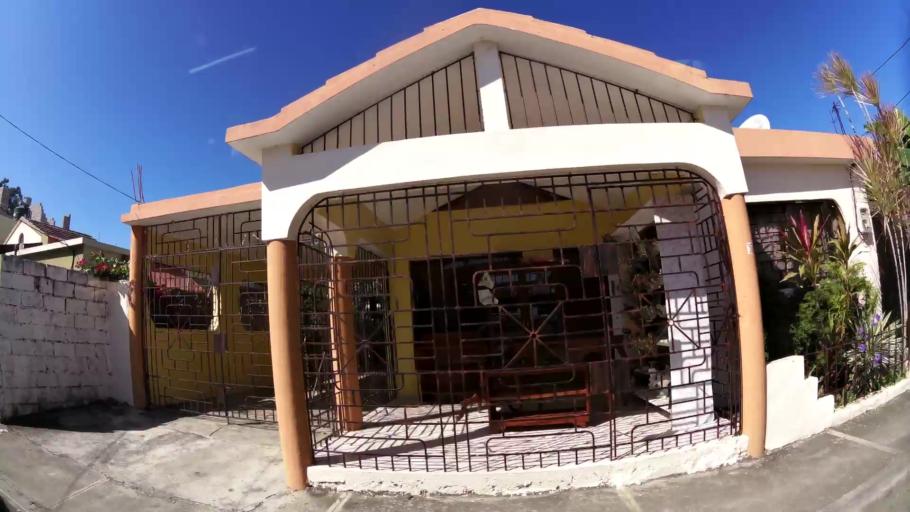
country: DO
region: San Cristobal
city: San Cristobal
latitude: 18.4319
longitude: -70.1194
